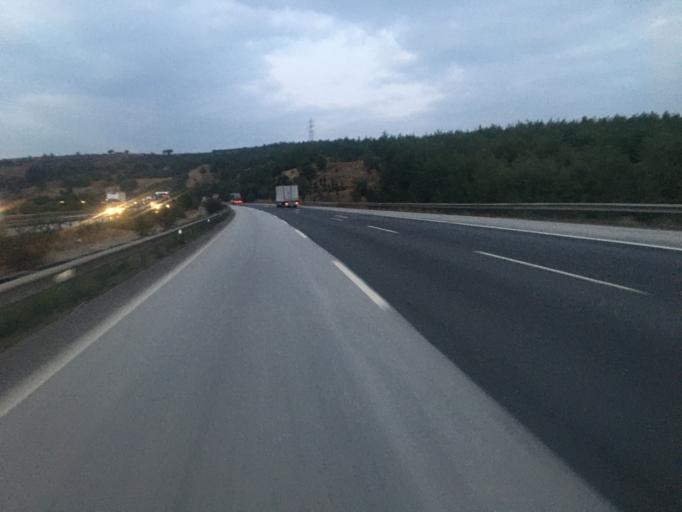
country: TR
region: Osmaniye
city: Haruniye
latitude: 37.1752
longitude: 36.3754
